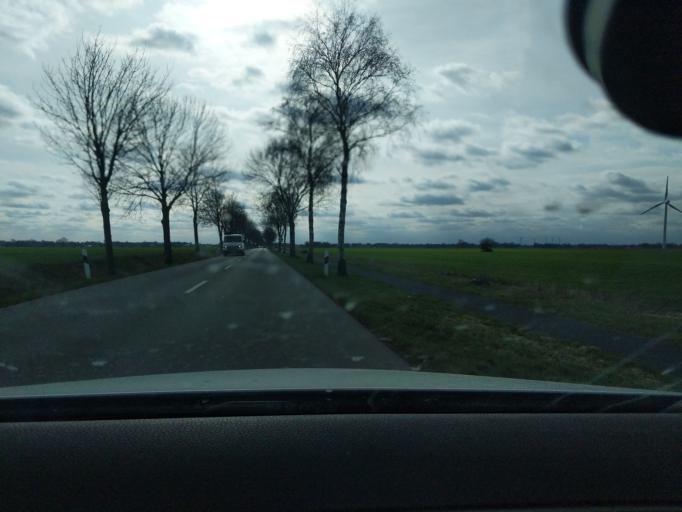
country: DE
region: Lower Saxony
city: Drochtersen
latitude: 53.6838
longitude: 9.3981
